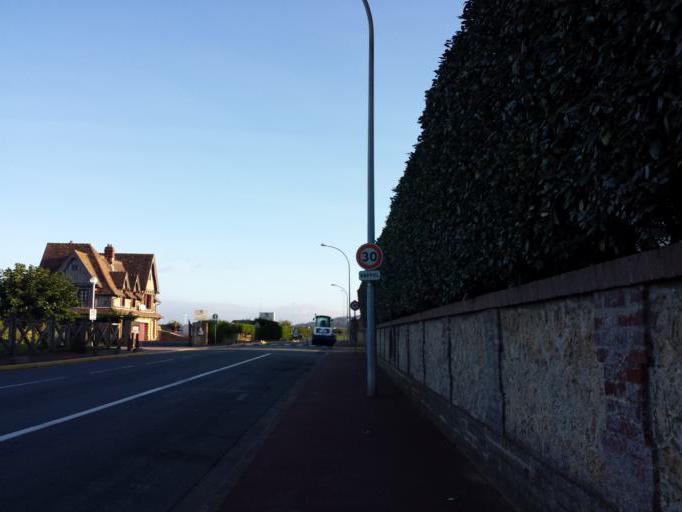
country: FR
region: Lower Normandy
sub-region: Departement du Calvados
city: Deauville
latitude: 49.3539
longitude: 0.0569
